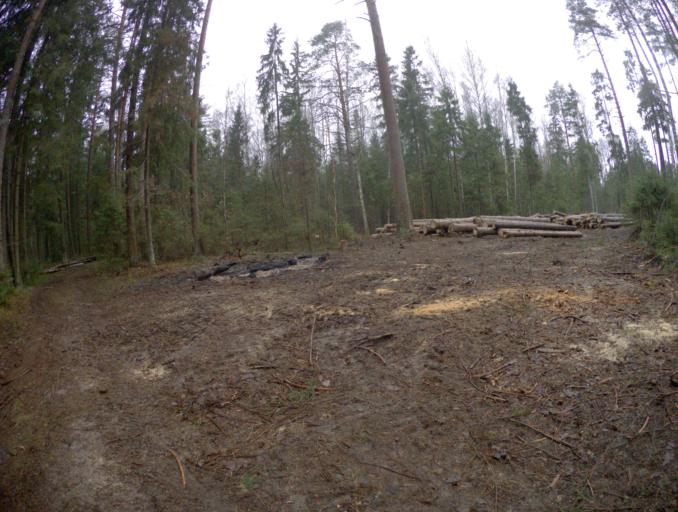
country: RU
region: Vladimir
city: Golovino
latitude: 56.0062
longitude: 40.4785
